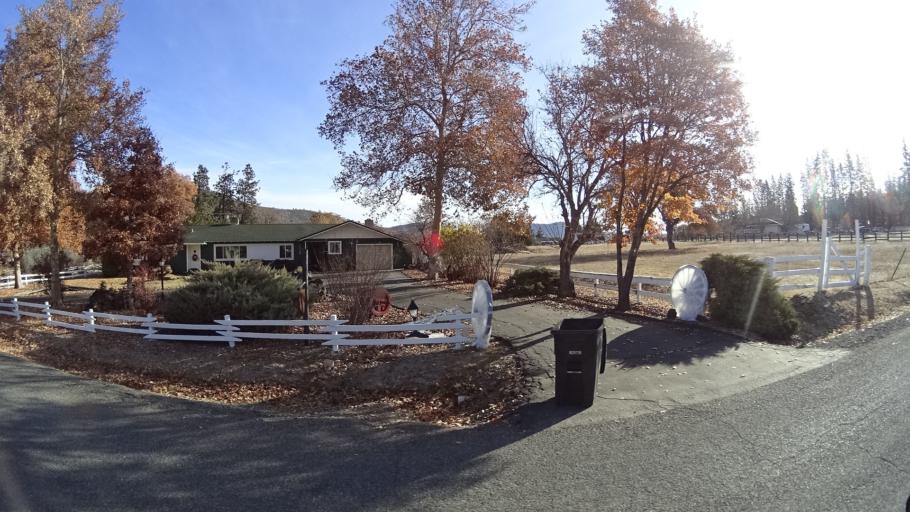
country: US
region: California
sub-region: Siskiyou County
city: Yreka
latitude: 41.6752
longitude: -122.6356
